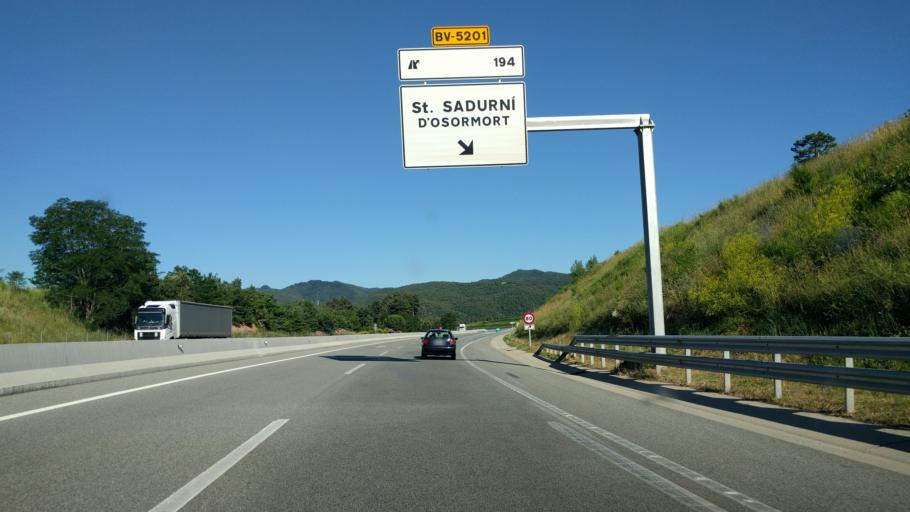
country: ES
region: Catalonia
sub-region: Provincia de Barcelona
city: Sant Julia de Vilatorta
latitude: 41.8935
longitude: 2.3516
